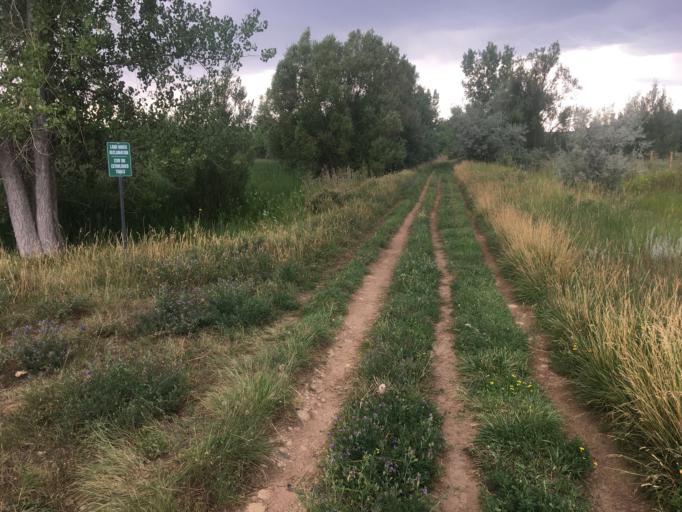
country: US
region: Colorado
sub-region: Boulder County
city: Boulder
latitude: 39.9707
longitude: -105.2316
